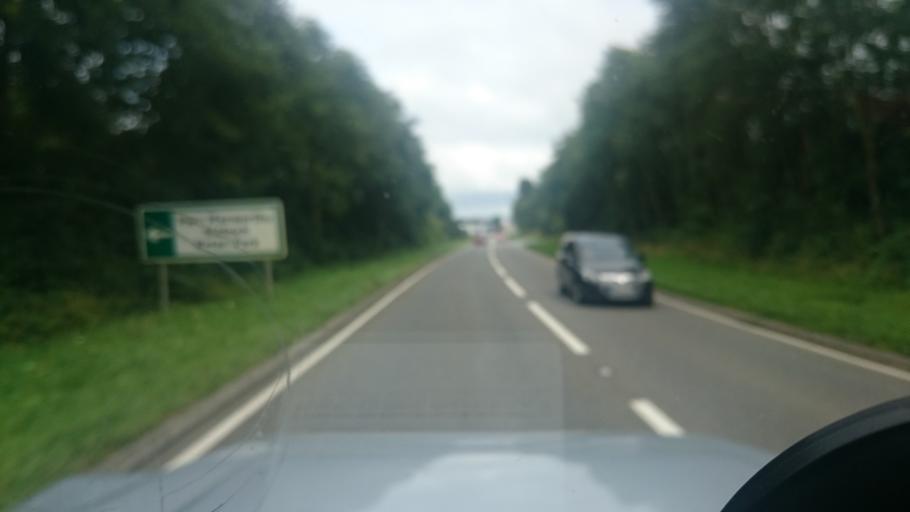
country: GB
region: Wales
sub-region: Pembrokeshire
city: Wiston
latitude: 51.8045
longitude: -4.8680
